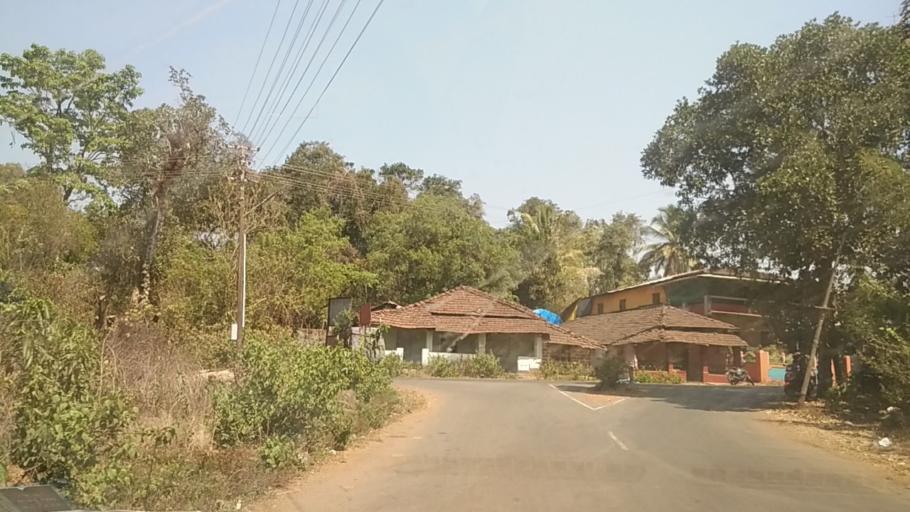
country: IN
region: Goa
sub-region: North Goa
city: Dicholi
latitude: 15.5794
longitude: 73.9208
